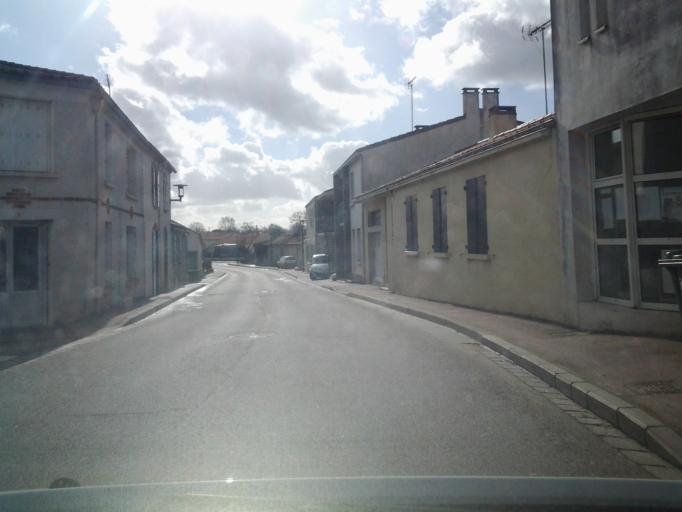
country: FR
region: Pays de la Loire
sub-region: Departement de la Vendee
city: Les Clouzeaux
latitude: 46.6287
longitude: -1.5085
